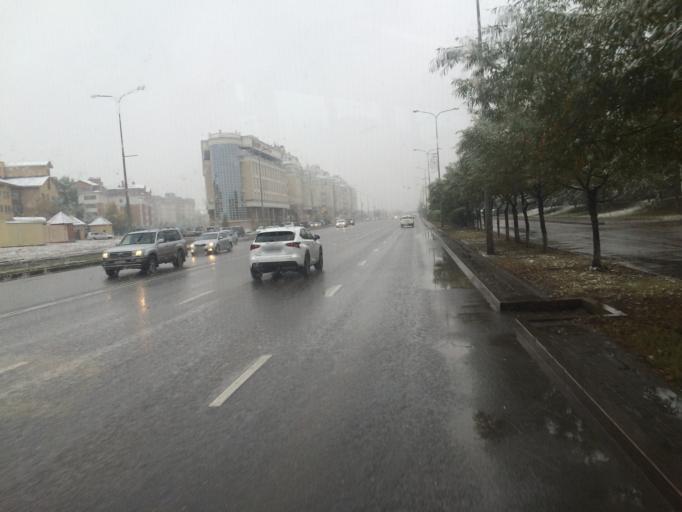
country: KZ
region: Astana Qalasy
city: Astana
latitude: 51.1463
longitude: 71.4447
